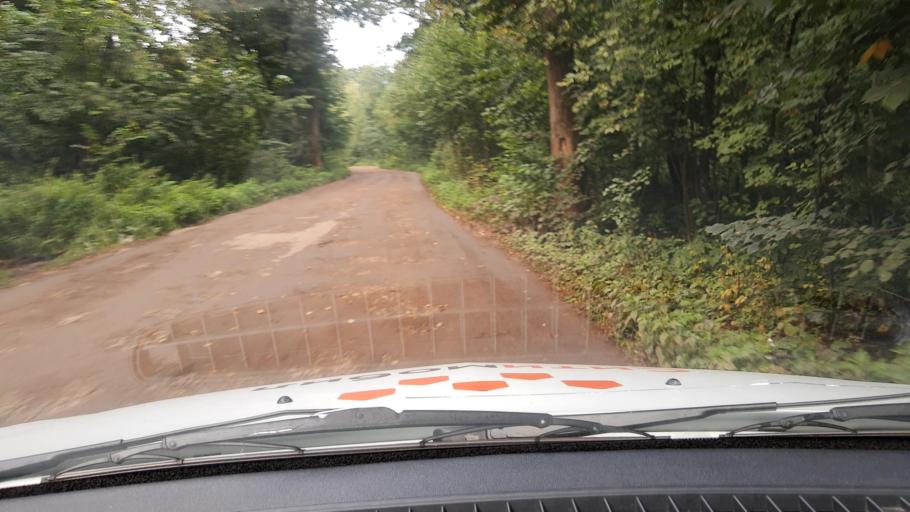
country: RU
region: Bashkortostan
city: Kabakovo
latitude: 54.7070
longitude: 56.1377
